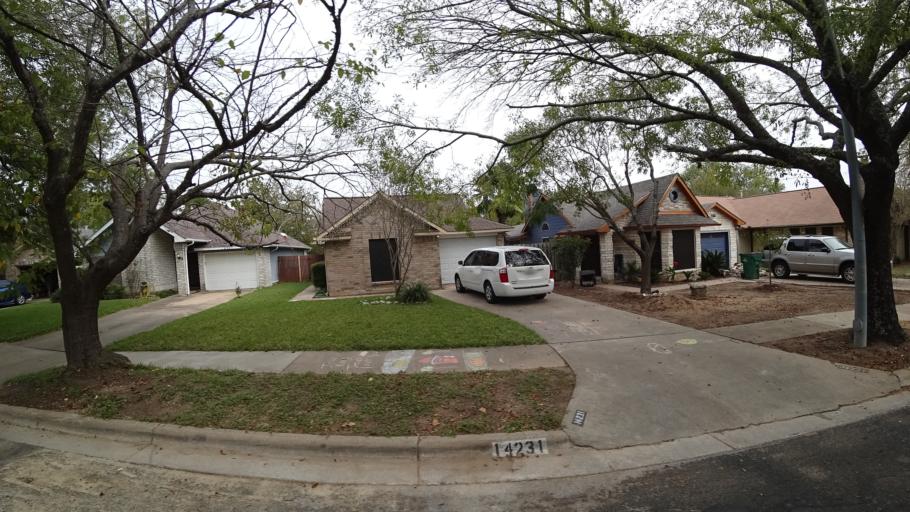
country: US
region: Texas
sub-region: Travis County
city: Wells Branch
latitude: 30.4385
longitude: -97.6836
